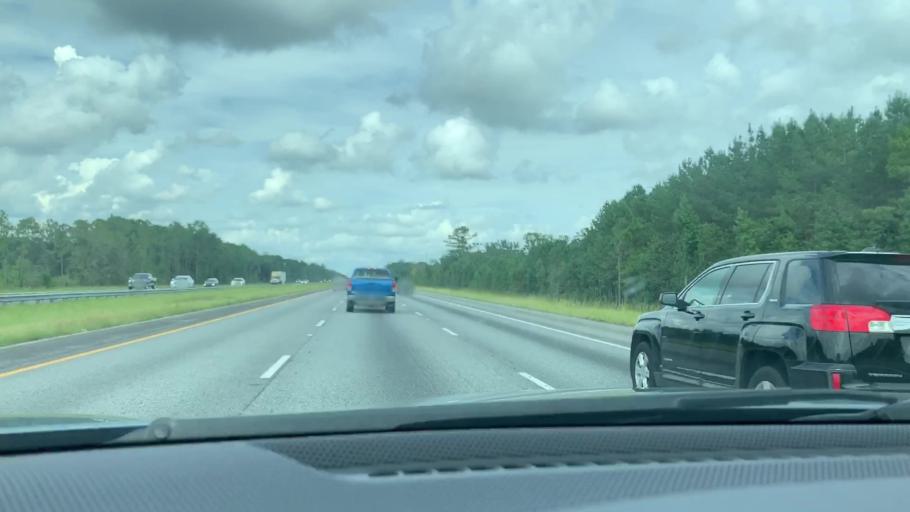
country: US
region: Georgia
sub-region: Liberty County
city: Midway
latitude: 31.6165
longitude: -81.4133
